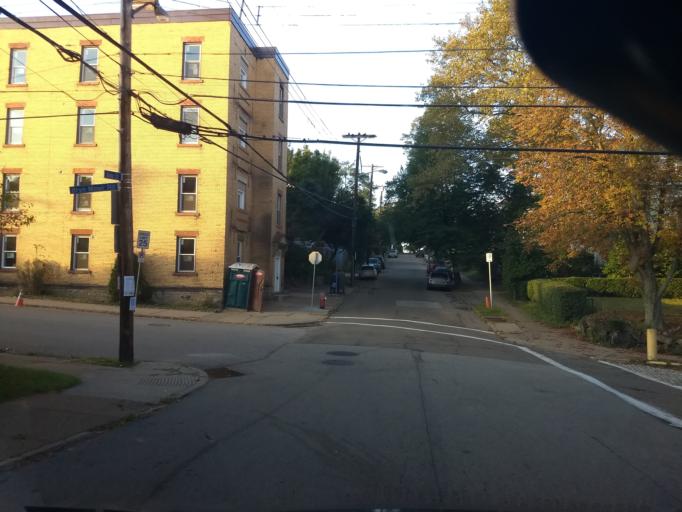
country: US
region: Pennsylvania
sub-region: Allegheny County
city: Bloomfield
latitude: 40.4513
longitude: -79.9573
